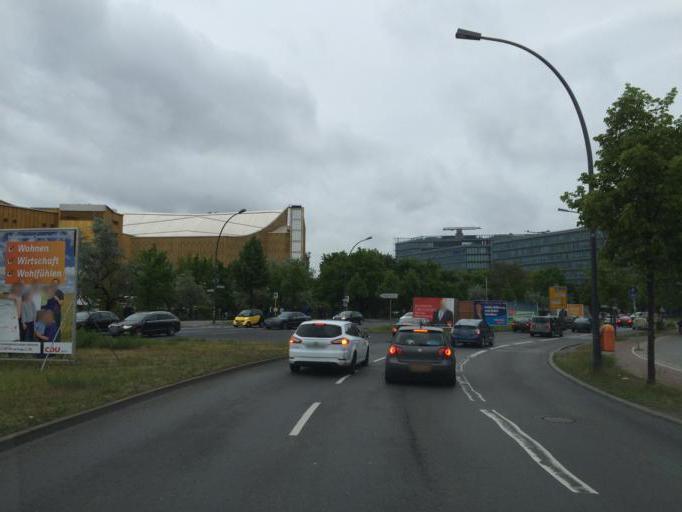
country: DE
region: Berlin
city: Tiergarten Bezirk
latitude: 52.5082
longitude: 13.3696
